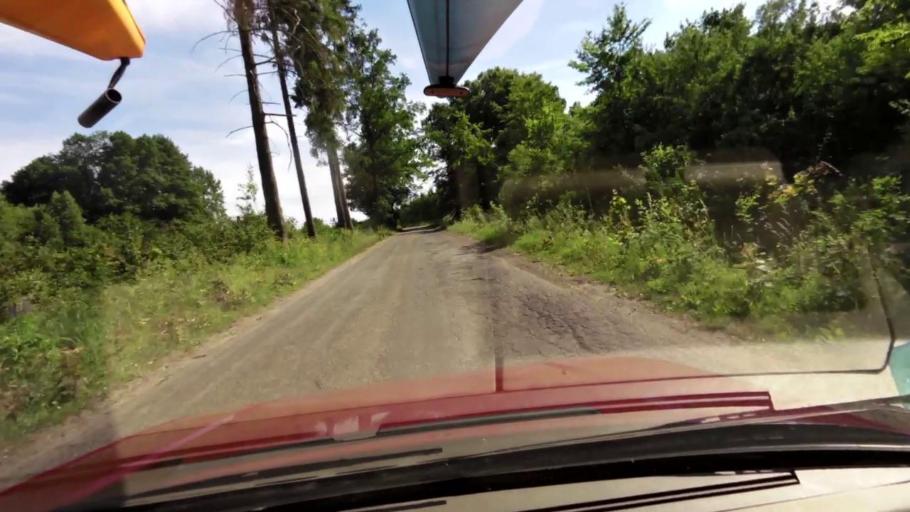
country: PL
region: Pomeranian Voivodeship
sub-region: Powiat slupski
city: Kepice
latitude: 54.1818
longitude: 16.8878
